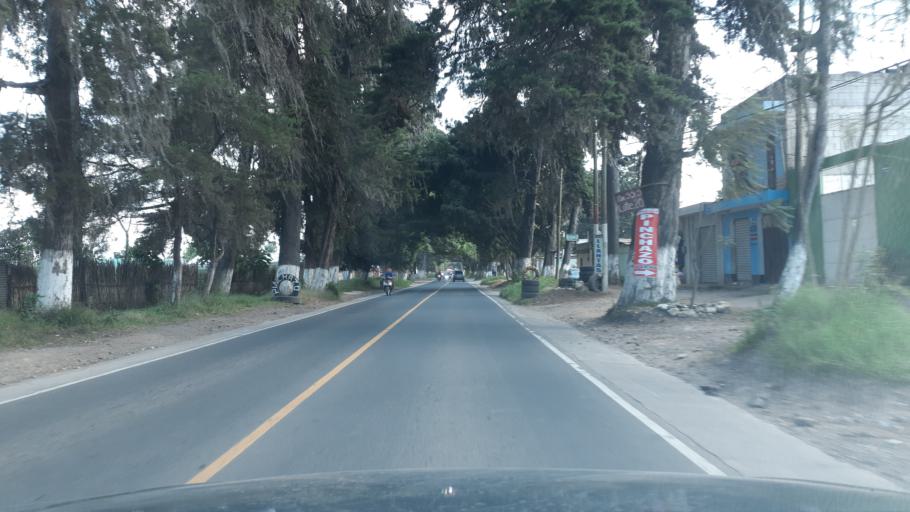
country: GT
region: Chimaltenango
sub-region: Municipio de Chimaltenango
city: Chimaltenango
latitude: 14.6466
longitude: -90.8121
